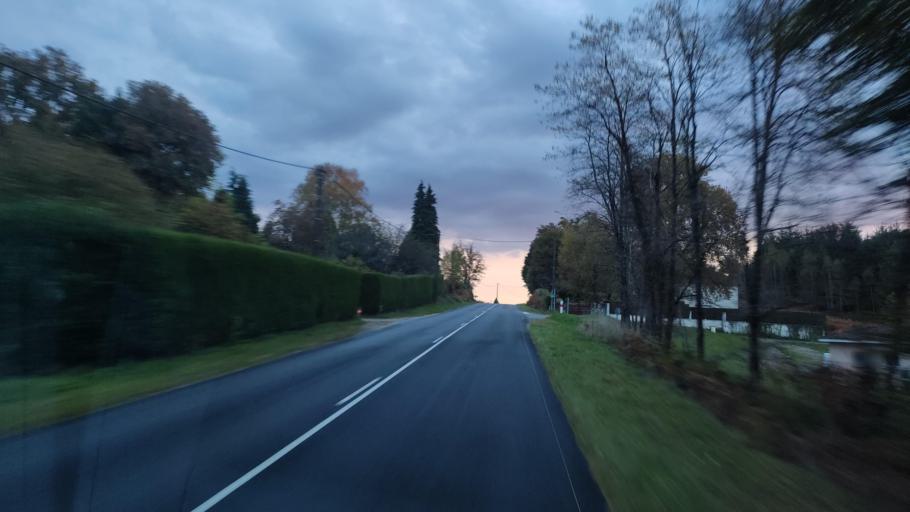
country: FR
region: Limousin
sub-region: Departement de la Haute-Vienne
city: Rilhac-Rancon
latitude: 45.9337
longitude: 1.3504
